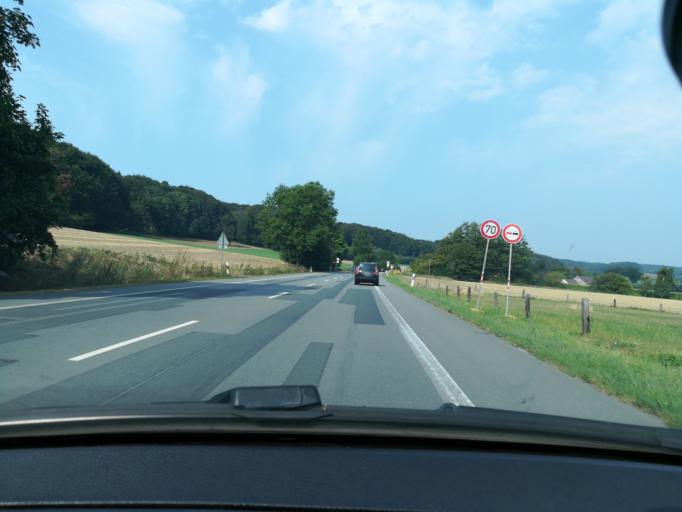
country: DE
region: North Rhine-Westphalia
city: Borgholzhausen
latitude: 52.1002
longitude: 8.3409
